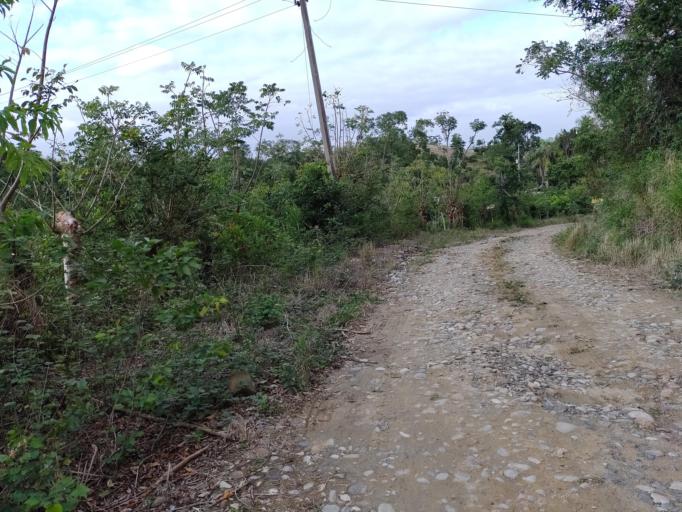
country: MX
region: Veracruz
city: Papantla de Olarte
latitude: 20.4496
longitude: -97.3085
